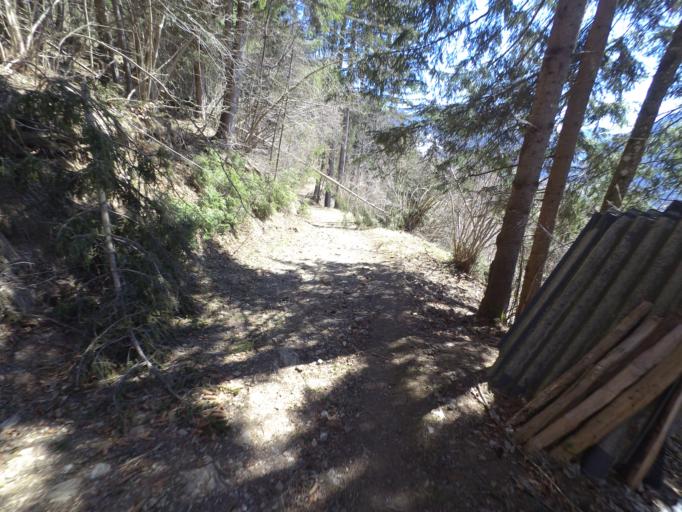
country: AT
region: Salzburg
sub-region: Politischer Bezirk Sankt Johann im Pongau
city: Sankt Veit im Pongau
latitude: 47.3354
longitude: 13.1602
